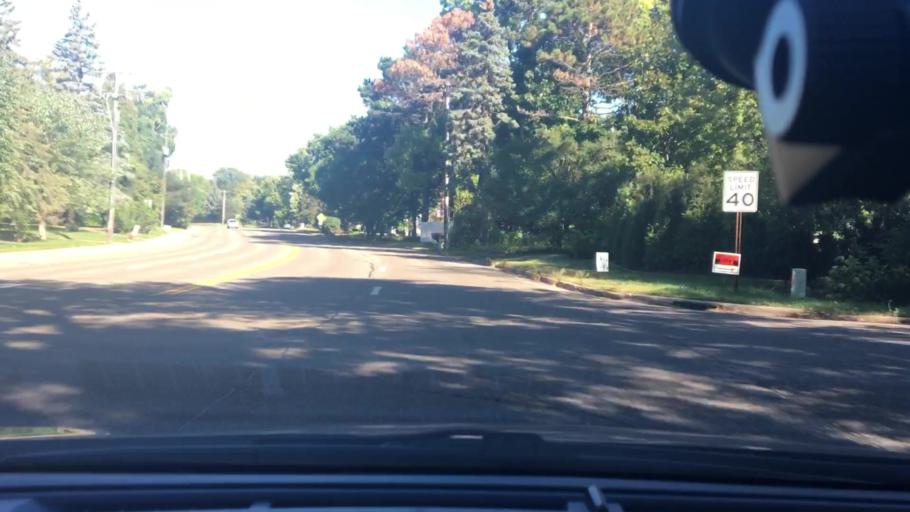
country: US
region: Minnesota
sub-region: Hennepin County
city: Minnetonka Mills
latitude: 44.9750
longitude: -93.4463
